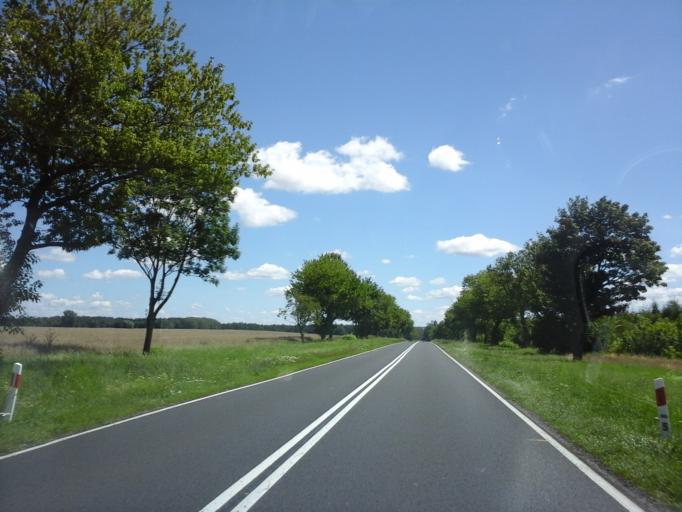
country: PL
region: West Pomeranian Voivodeship
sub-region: Powiat choszczenski
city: Recz
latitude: 53.2665
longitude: 15.5114
